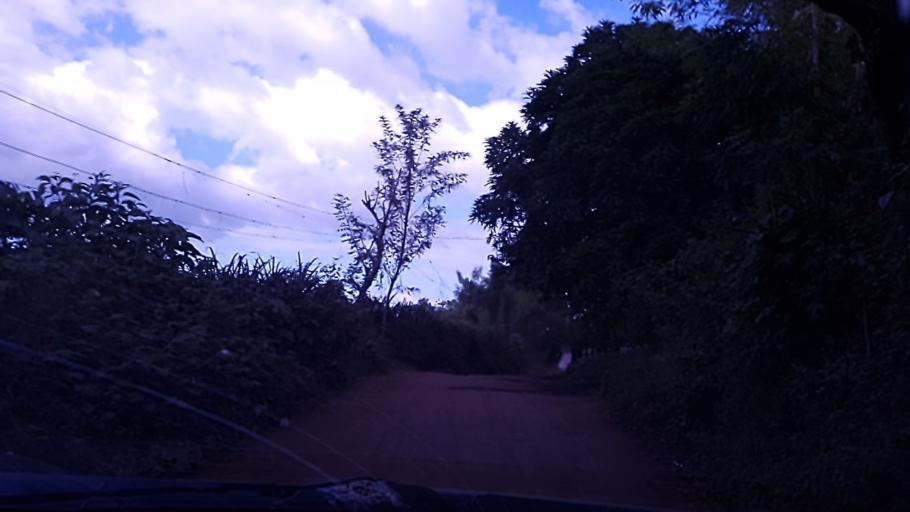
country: NI
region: Masaya
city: Ticuantepe
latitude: 11.9950
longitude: -86.2245
